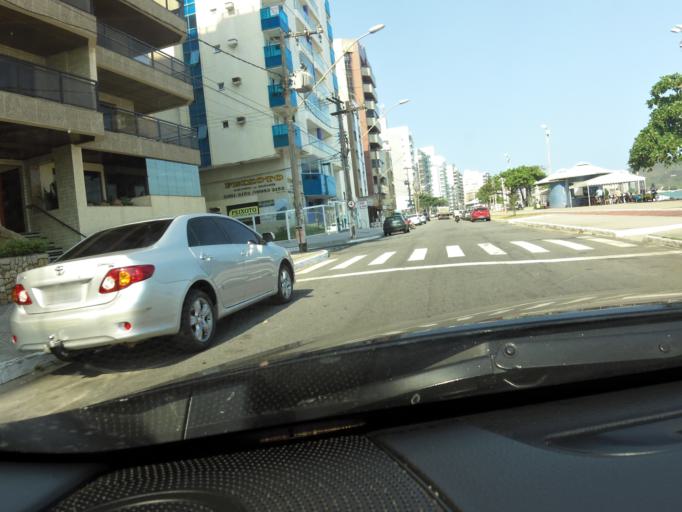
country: BR
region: Espirito Santo
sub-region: Guarapari
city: Guarapari
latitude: -20.6526
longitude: -40.4840
